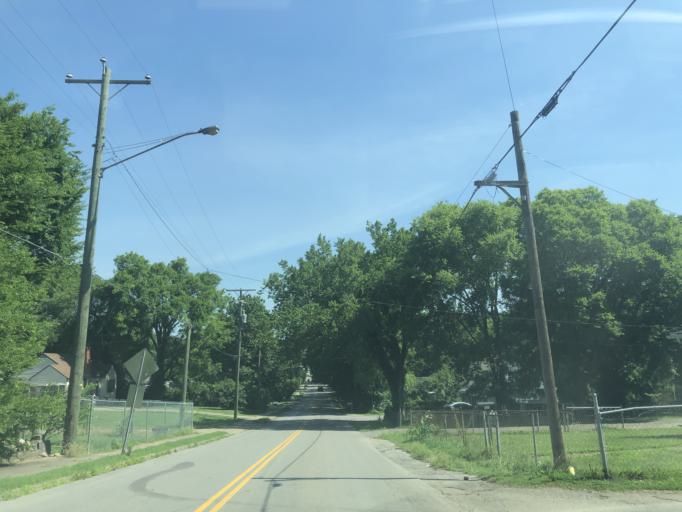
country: US
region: Tennessee
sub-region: Davidson County
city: Nashville
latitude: 36.2020
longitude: -86.7663
